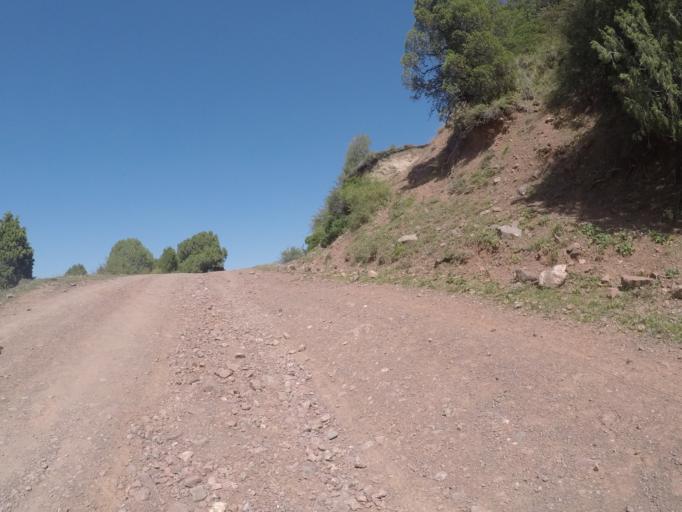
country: KG
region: Chuy
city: Bishkek
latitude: 42.6467
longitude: 74.5664
